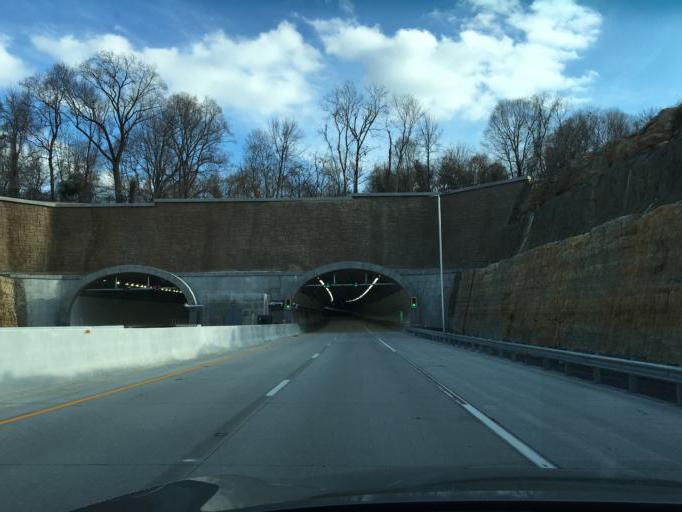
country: US
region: Kentucky
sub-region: Jefferson County
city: Prospect
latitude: 38.3276
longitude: -85.6257
